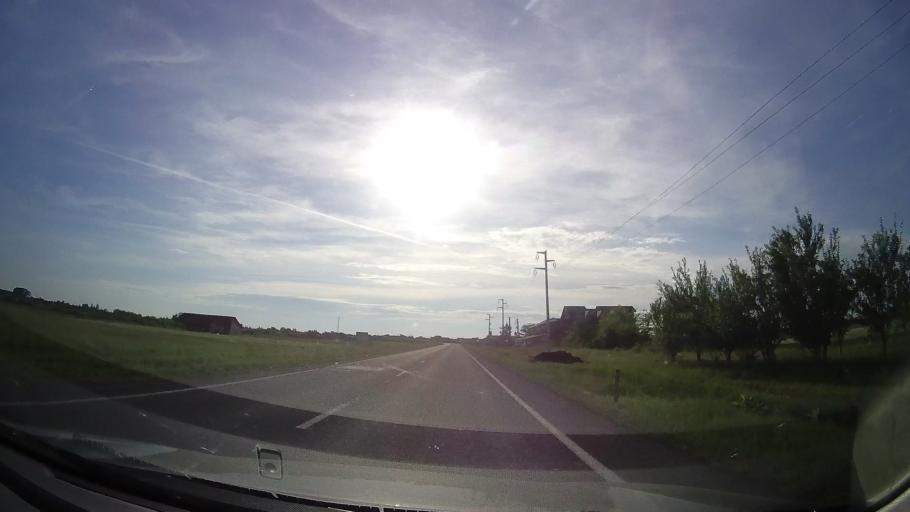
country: RO
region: Timis
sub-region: Oras Recas
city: Izvin
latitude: 45.8017
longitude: 21.4782
